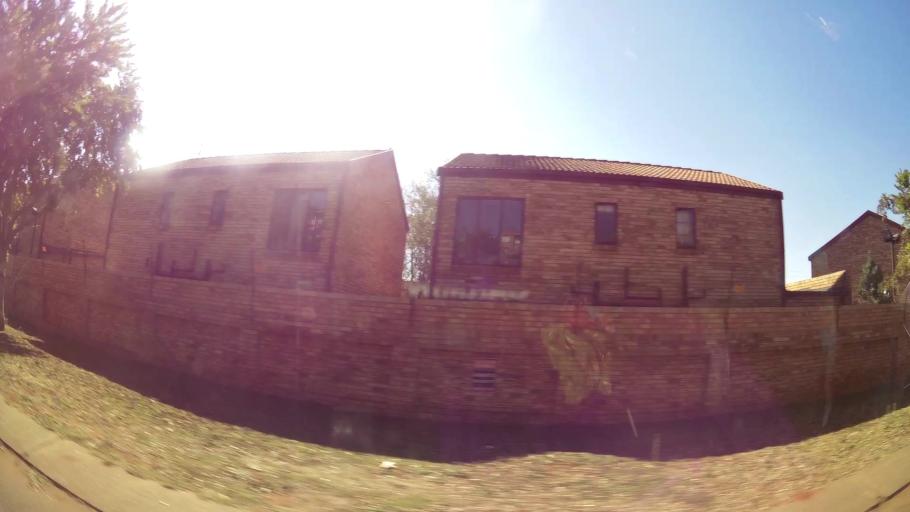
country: ZA
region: Gauteng
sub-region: City of Tshwane Metropolitan Municipality
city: Centurion
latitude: -25.8534
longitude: 28.1801
